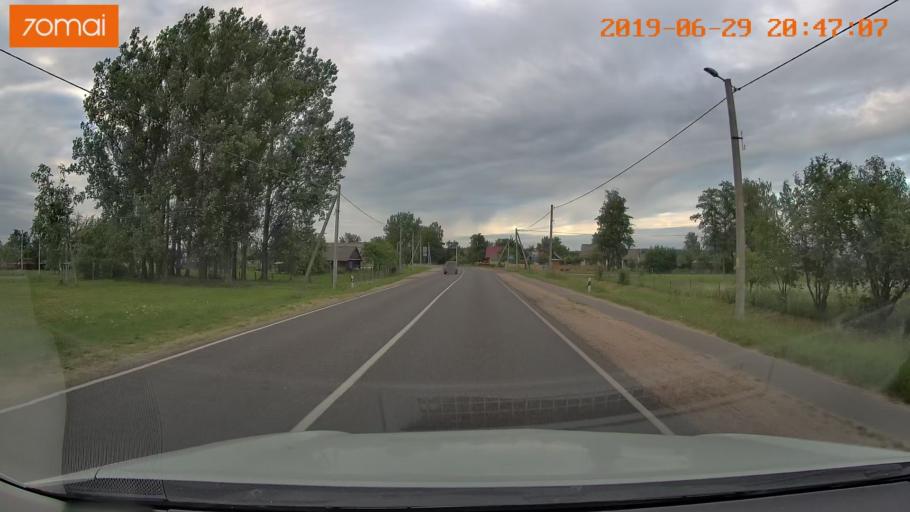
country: BY
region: Brest
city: Hantsavichy
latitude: 52.6353
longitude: 26.3146
